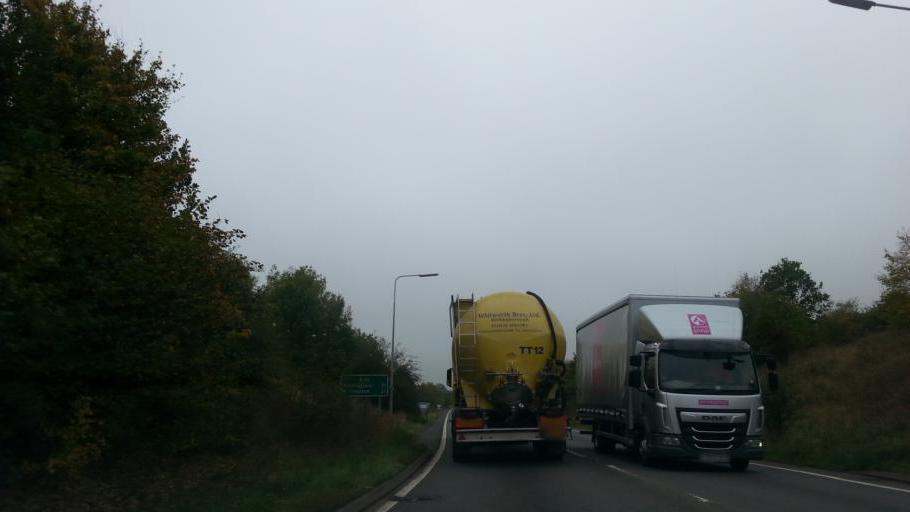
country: GB
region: England
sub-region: Northamptonshire
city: Thrapston
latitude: 52.3907
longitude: -0.5233
